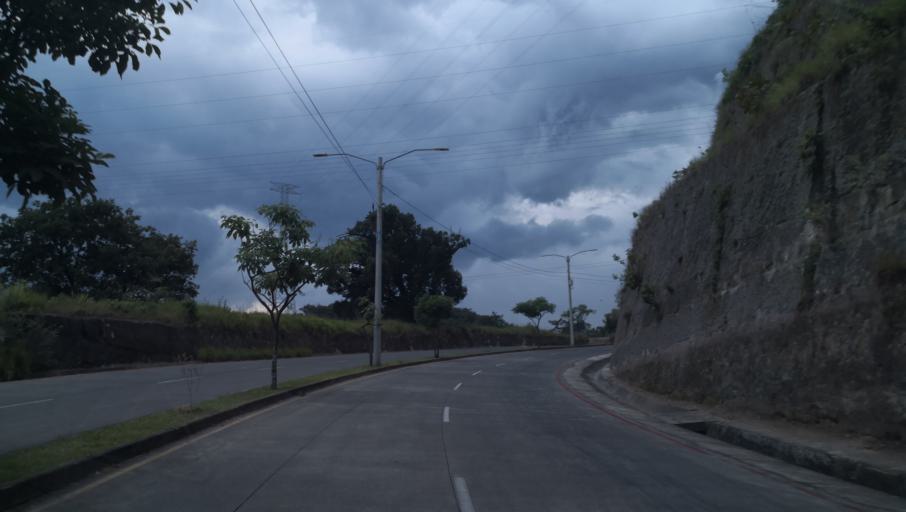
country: GT
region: Guatemala
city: Villa Nueva
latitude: 14.5543
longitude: -90.5946
